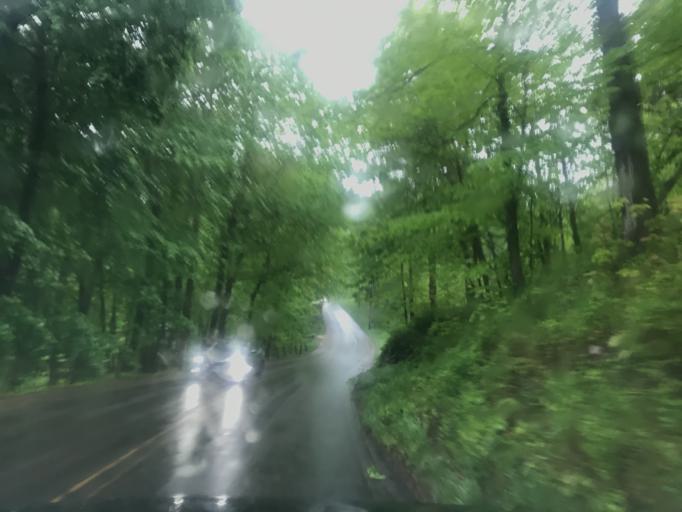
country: US
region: Connecticut
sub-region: Fairfield County
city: Bethel
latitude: 41.3062
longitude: -73.3738
